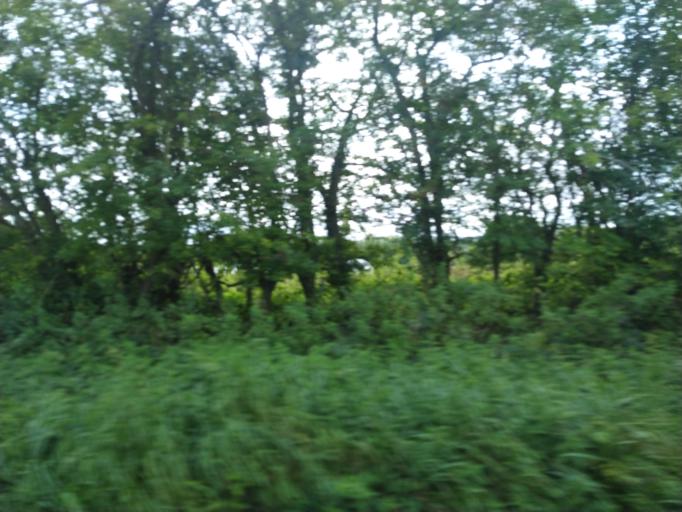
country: GB
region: England
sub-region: Dorset
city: Blandford Forum
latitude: 50.8330
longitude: -2.1217
